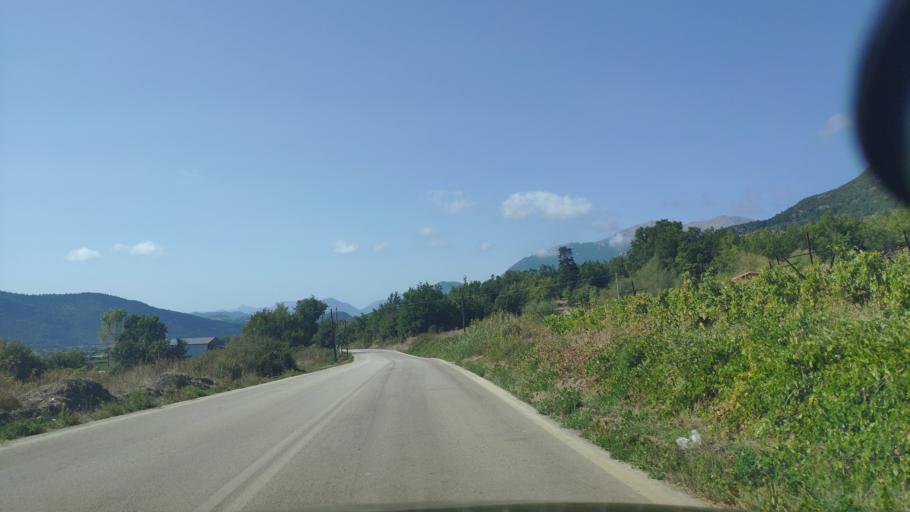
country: GR
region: Peloponnese
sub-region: Nomos Korinthias
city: Xylokastro
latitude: 37.9608
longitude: 22.5812
